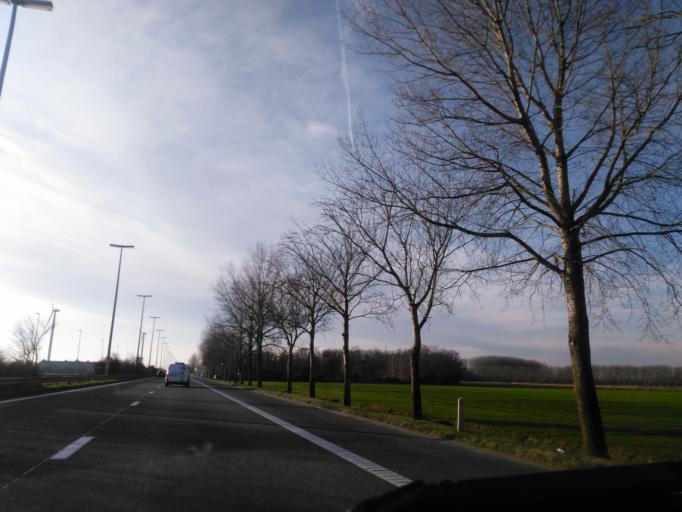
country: BE
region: Flanders
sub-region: Provincie Oost-Vlaanderen
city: Sint-Gillis-Waas
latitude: 51.2333
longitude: 4.1410
